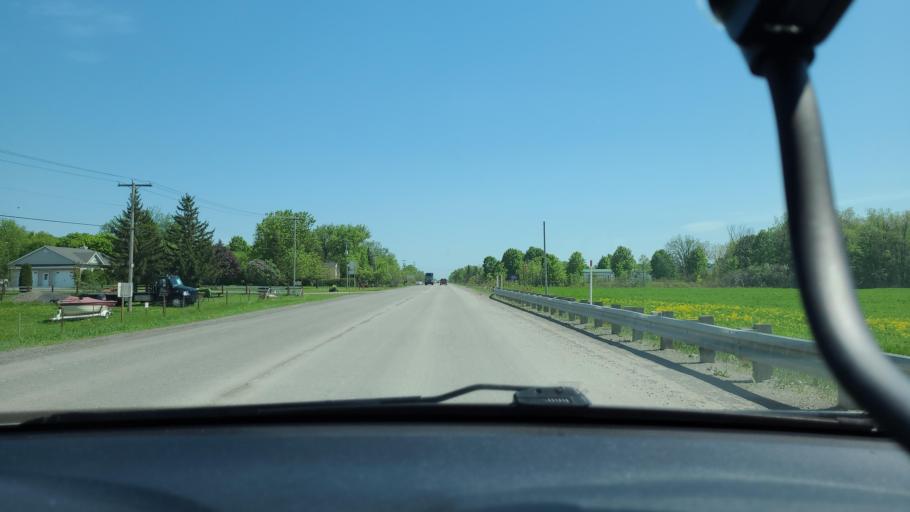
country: CA
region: Quebec
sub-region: Laurentides
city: Saint-Colomban
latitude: 45.6591
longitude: -74.1623
